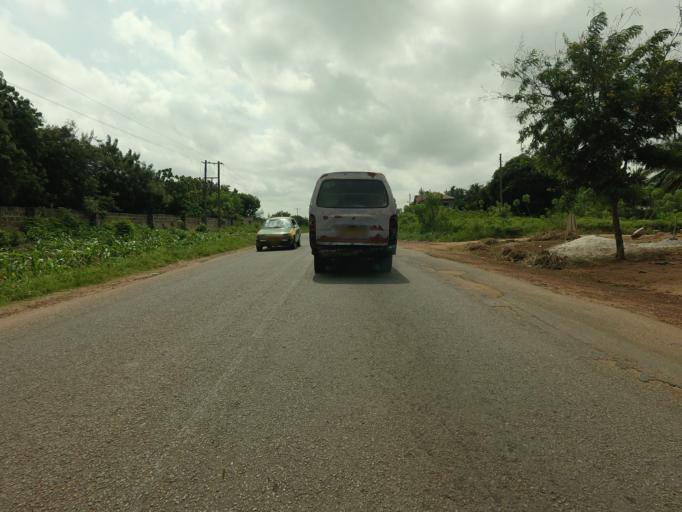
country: TG
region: Maritime
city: Lome
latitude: 6.1253
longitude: 1.1262
